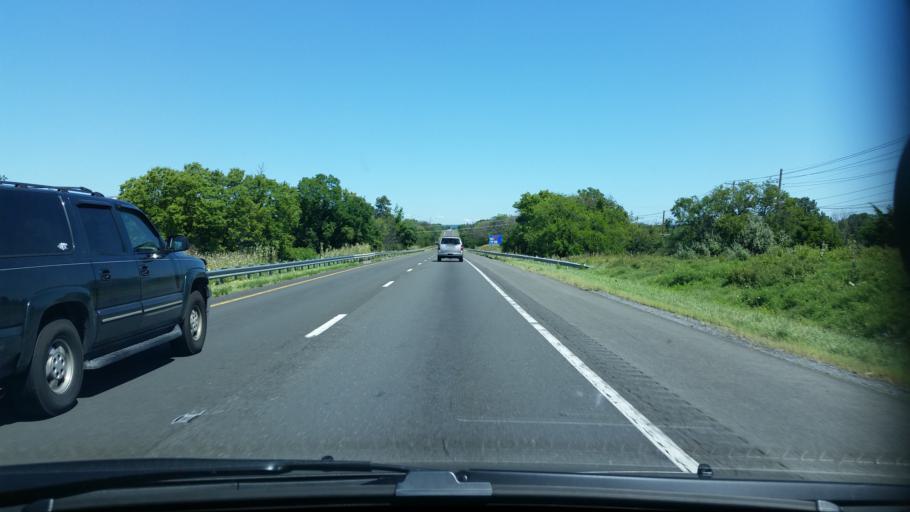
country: US
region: Virginia
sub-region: City of Winchester
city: Winchester
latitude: 39.2009
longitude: -78.1342
